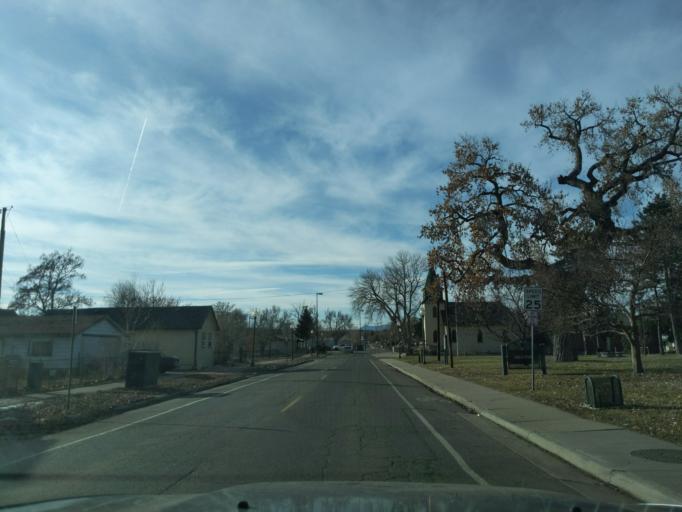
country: US
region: Colorado
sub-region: Denver County
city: Denver
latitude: 39.7819
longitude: -104.9813
